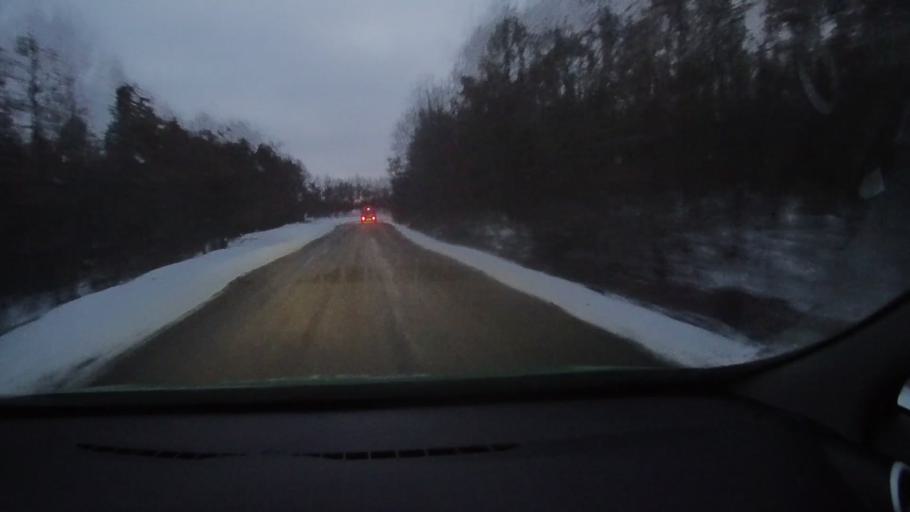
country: RO
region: Harghita
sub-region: Comuna Darjiu
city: Darjiu
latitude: 46.1808
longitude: 25.2490
